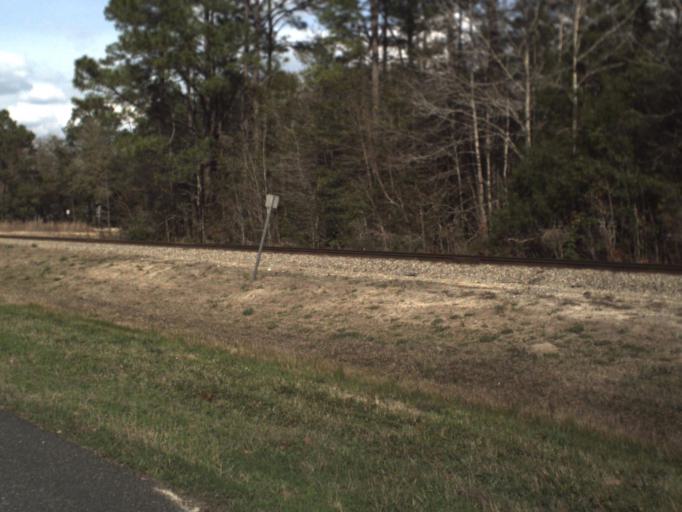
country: US
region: Florida
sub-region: Bay County
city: Youngstown
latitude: 30.4762
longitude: -85.4210
